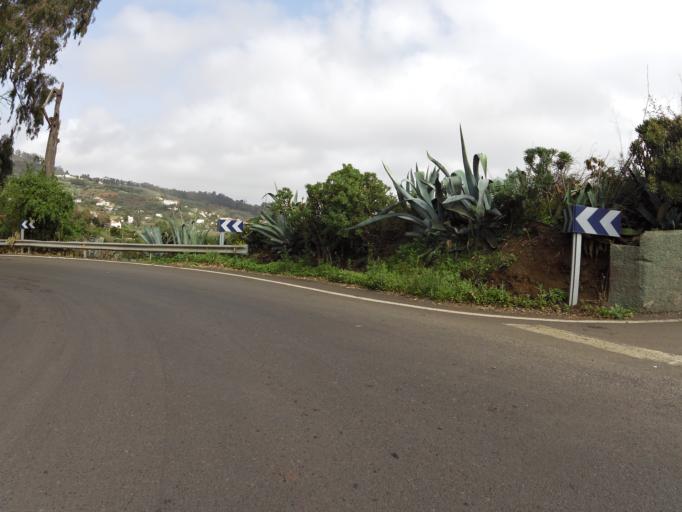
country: ES
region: Canary Islands
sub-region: Provincia de Las Palmas
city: Teror
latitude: 28.0761
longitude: -15.5386
